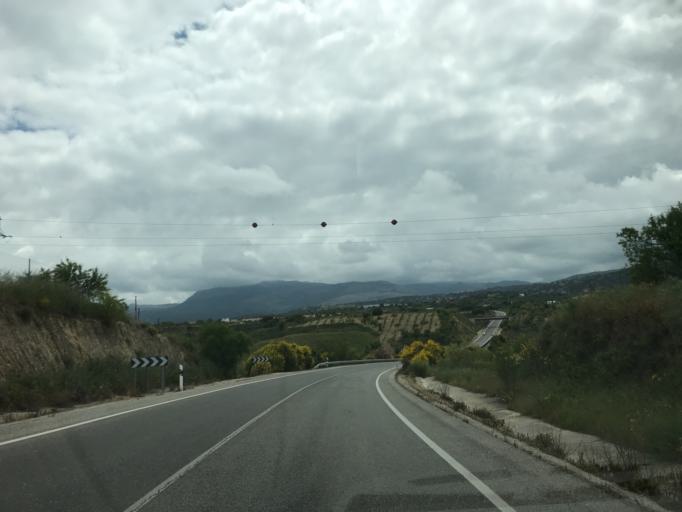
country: ES
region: Andalusia
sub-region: Provincia de Malaga
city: Ronda
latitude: 36.7254
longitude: -5.1647
